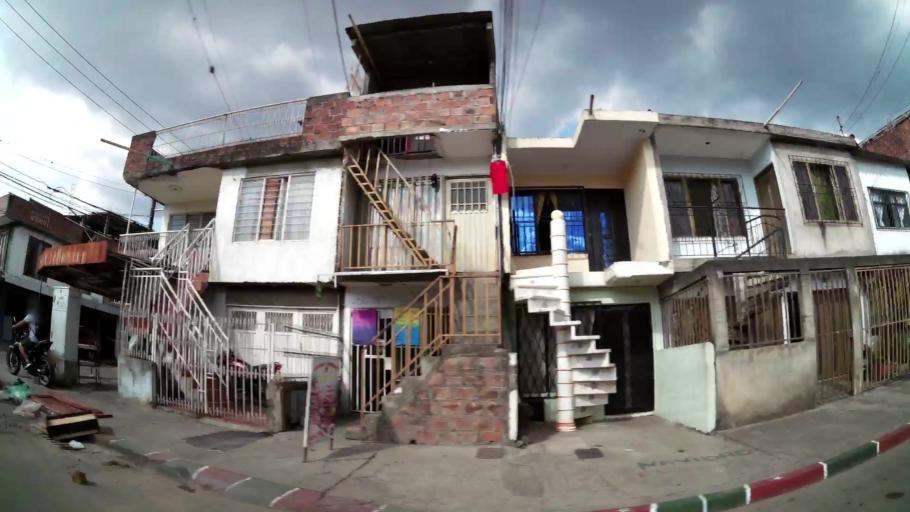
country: CO
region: Valle del Cauca
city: Cali
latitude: 3.4067
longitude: -76.4961
